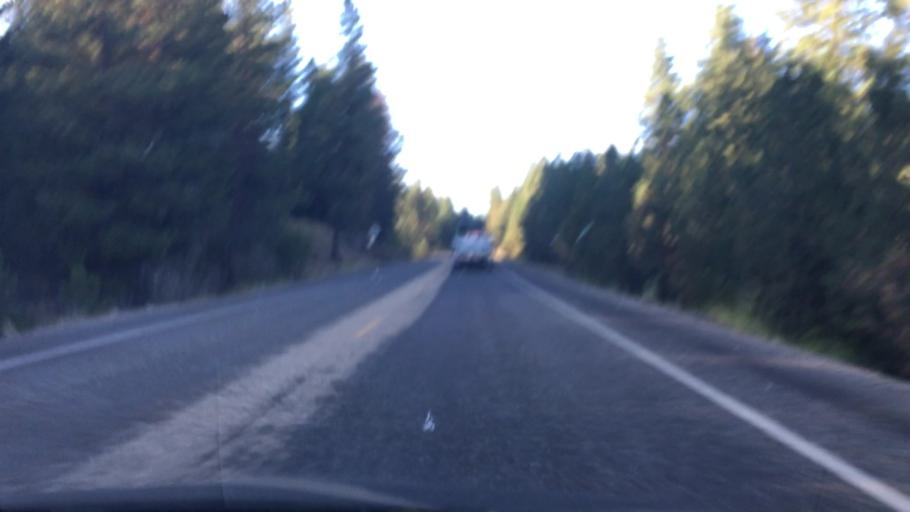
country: US
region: Idaho
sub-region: Valley County
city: Cascade
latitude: 44.5609
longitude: -116.0293
